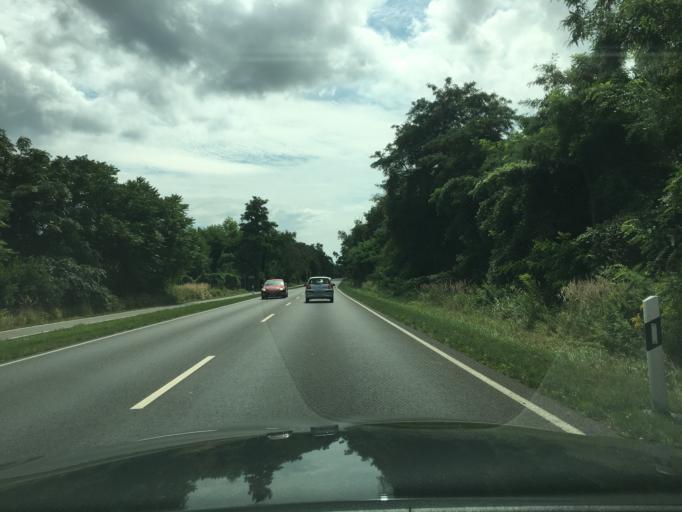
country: DE
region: Saxony-Anhalt
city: Sandersdorf
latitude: 51.6303
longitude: 12.2820
